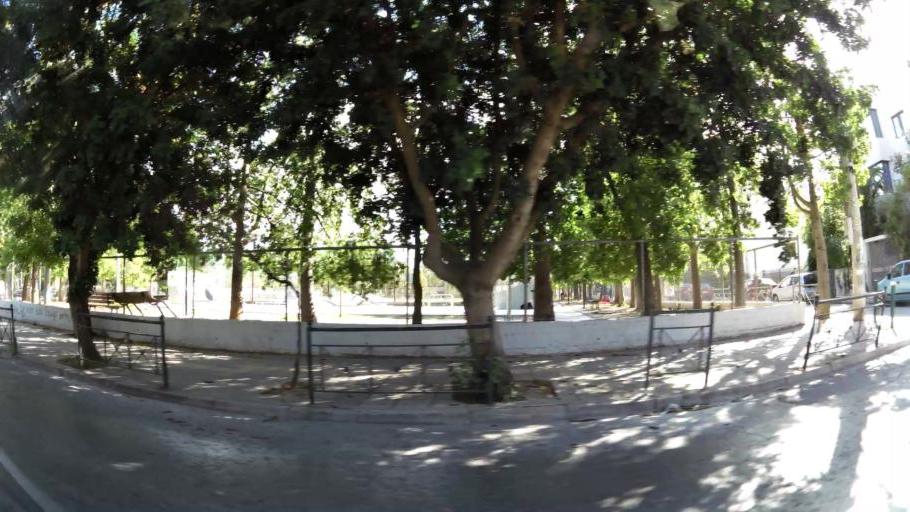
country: GR
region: Attica
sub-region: Nomarchia Athinas
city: Khalandrion
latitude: 38.0124
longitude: 23.7969
